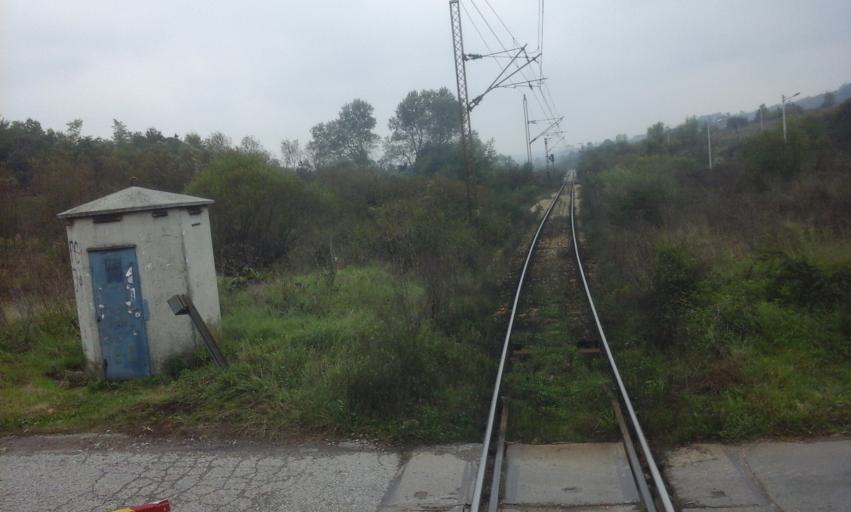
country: RS
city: Rusanj
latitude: 44.6366
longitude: 20.5336
